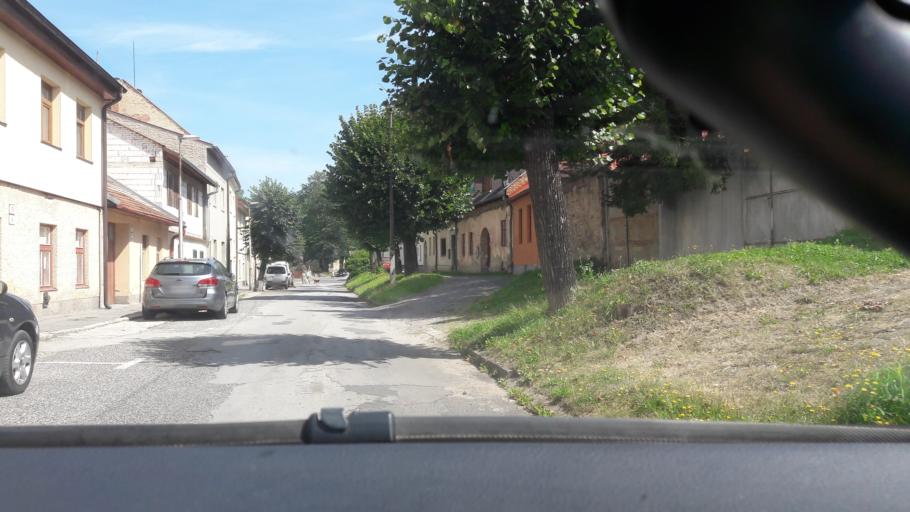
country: SK
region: Presovsky
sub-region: Okres Presov
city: Kezmarok
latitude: 49.1388
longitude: 20.4314
